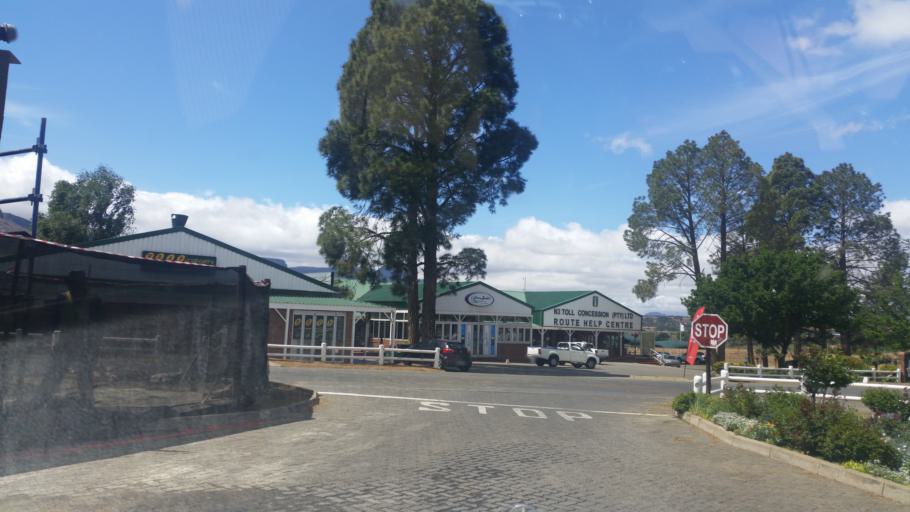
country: ZA
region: Orange Free State
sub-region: Thabo Mofutsanyana District Municipality
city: Harrismith
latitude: -28.2551
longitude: 29.1161
